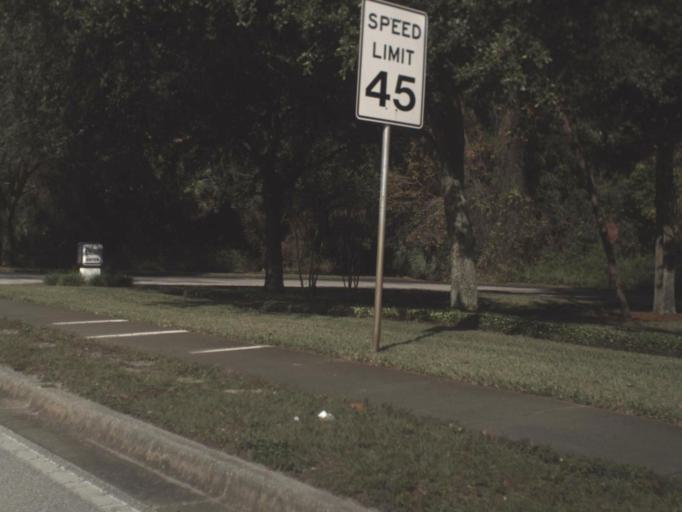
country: US
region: Florida
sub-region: Volusia County
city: Port Orange
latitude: 29.1304
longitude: -81.0263
